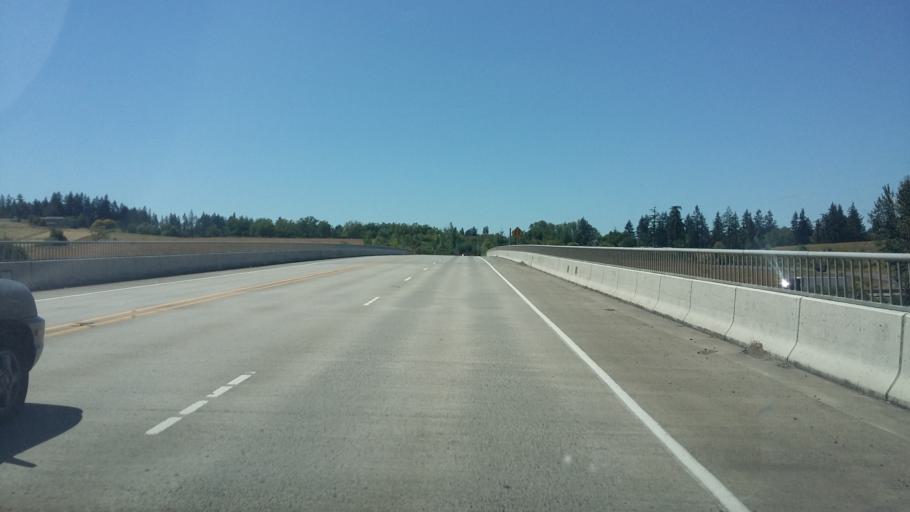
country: US
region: Washington
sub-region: Clark County
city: Mount Vista
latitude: 45.7809
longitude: -122.6720
